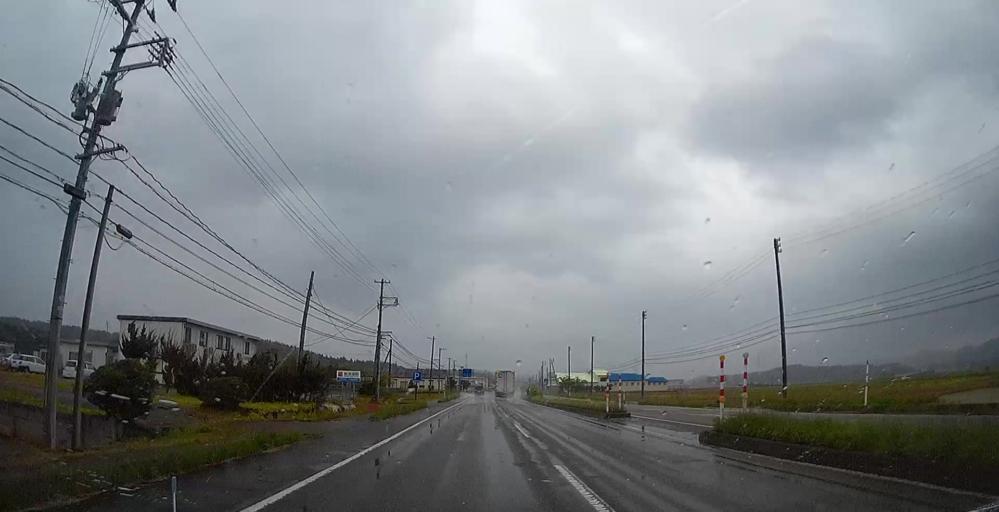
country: JP
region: Niigata
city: Kashiwazaki
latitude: 37.4278
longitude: 138.6218
